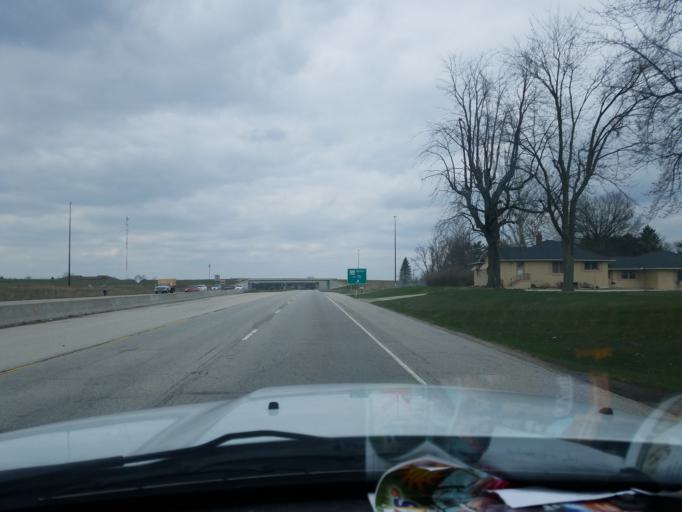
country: US
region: Indiana
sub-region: Vigo County
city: Terre Haute
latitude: 39.3660
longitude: -87.3882
